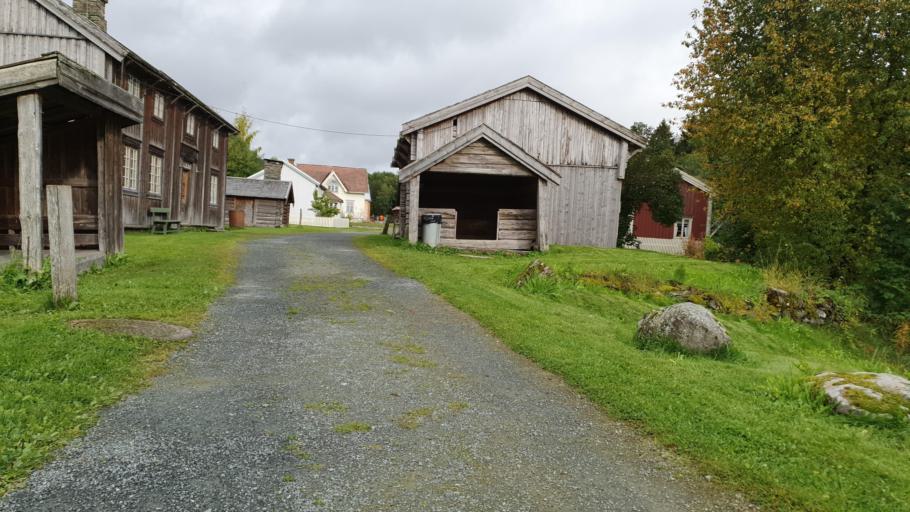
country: NO
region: Nord-Trondelag
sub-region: Verdal
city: Verdal
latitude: 63.7979
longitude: 11.5659
